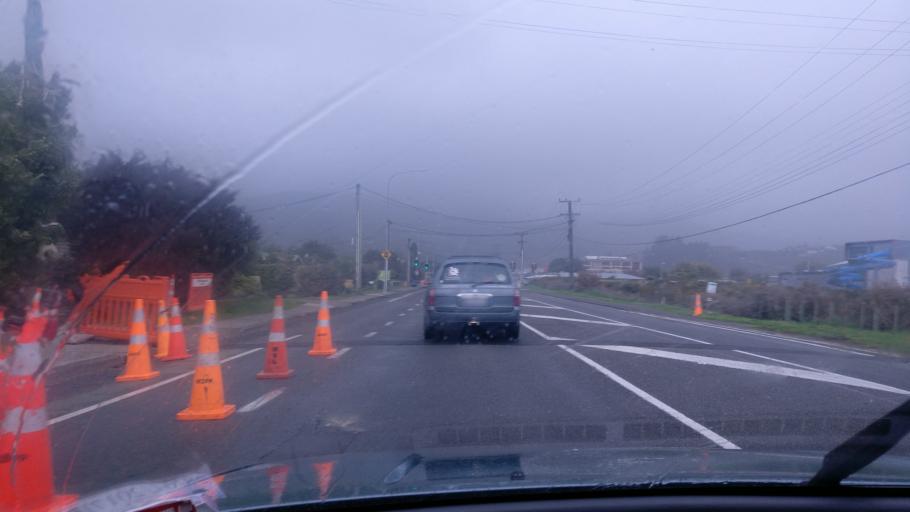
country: NZ
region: Wellington
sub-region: Kapiti Coast District
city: Paraparaumu
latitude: -40.9106
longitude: 175.0020
